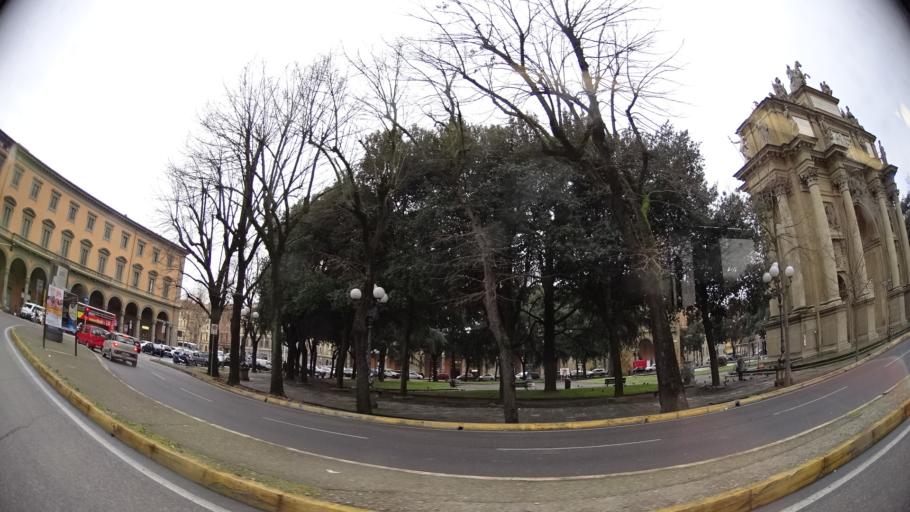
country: IT
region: Tuscany
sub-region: Province of Florence
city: Florence
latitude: 43.7857
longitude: 11.2648
